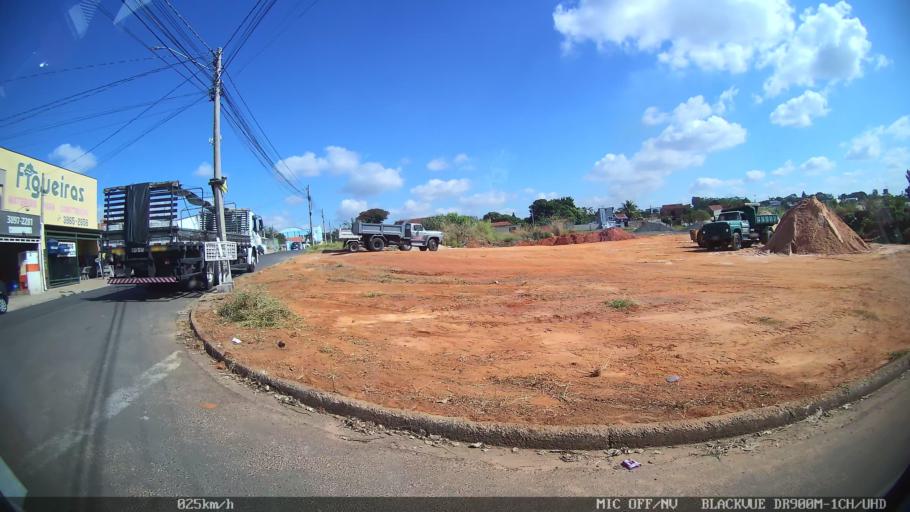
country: BR
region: Sao Paulo
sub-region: Hortolandia
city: Hortolandia
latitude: -22.8849
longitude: -47.2212
